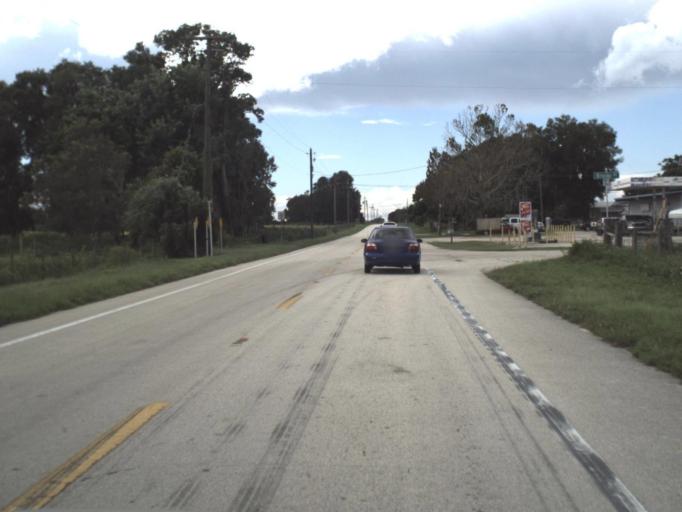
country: US
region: Florida
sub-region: Polk County
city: Fort Meade
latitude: 27.7481
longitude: -81.7428
